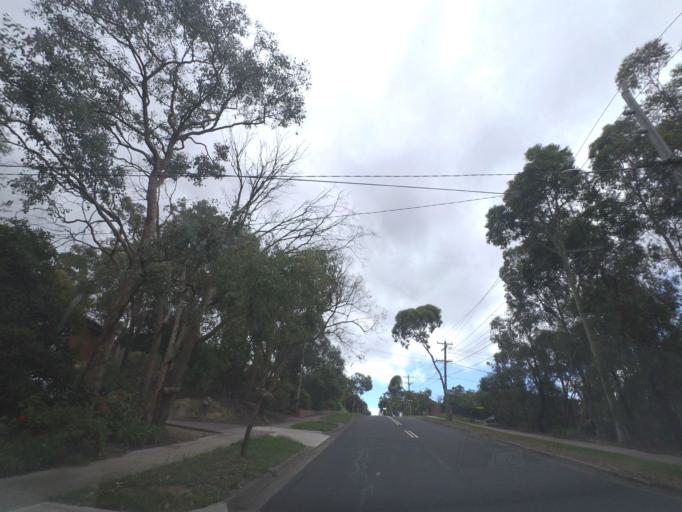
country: AU
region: Victoria
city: Mitcham
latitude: -37.8264
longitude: 145.2087
